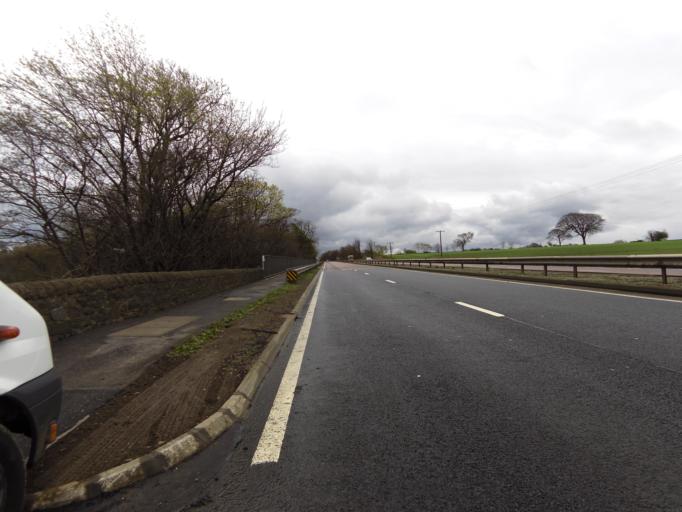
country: GB
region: Scotland
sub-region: Edinburgh
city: Queensferry
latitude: 55.9761
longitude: -3.3389
